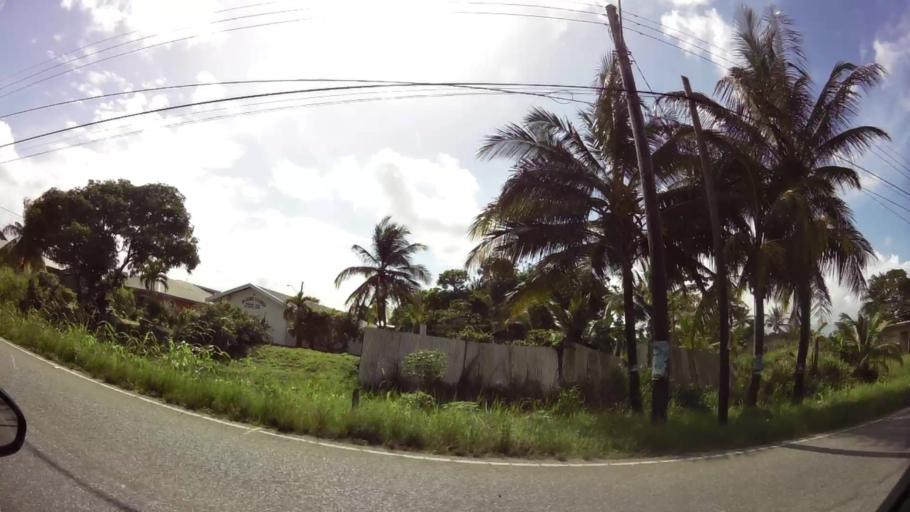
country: TT
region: Borough of Arima
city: Arima
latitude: 10.6221
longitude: -61.2560
